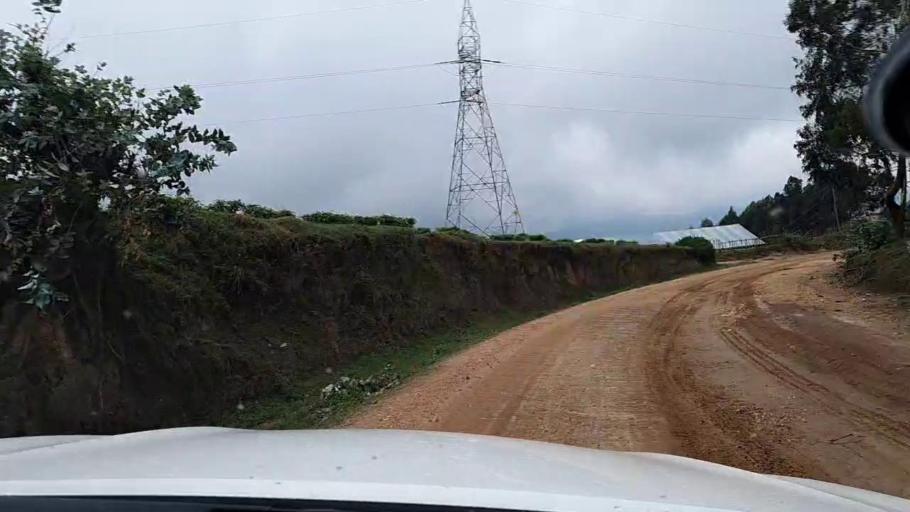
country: RW
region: Western Province
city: Kibuye
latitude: -2.2478
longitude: 29.3446
